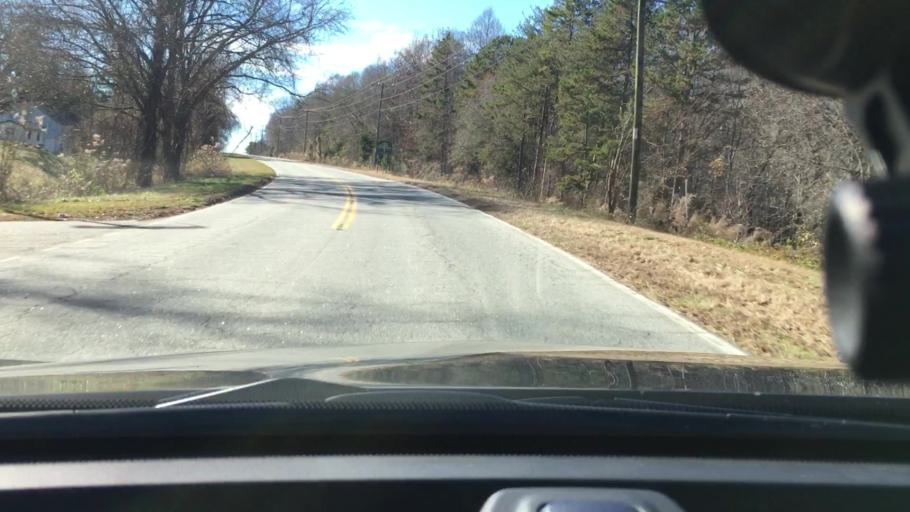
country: US
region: South Carolina
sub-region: Spartanburg County
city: Pacolet
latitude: 34.9304
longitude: -81.7368
